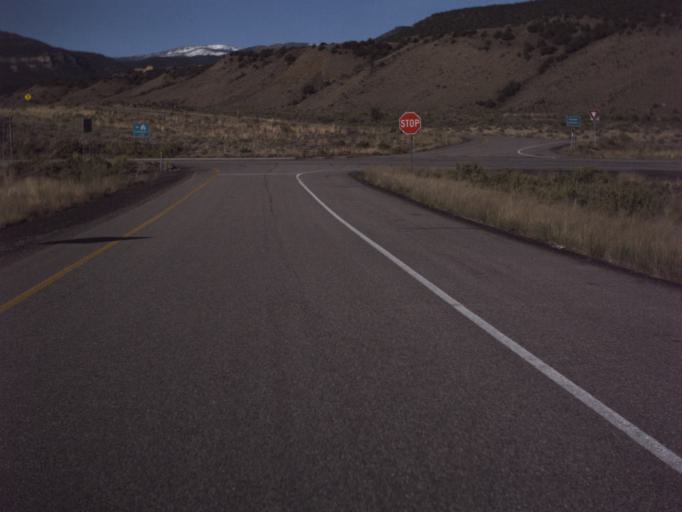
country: US
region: Utah
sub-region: Emery County
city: Ferron
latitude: 38.7668
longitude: -111.3482
